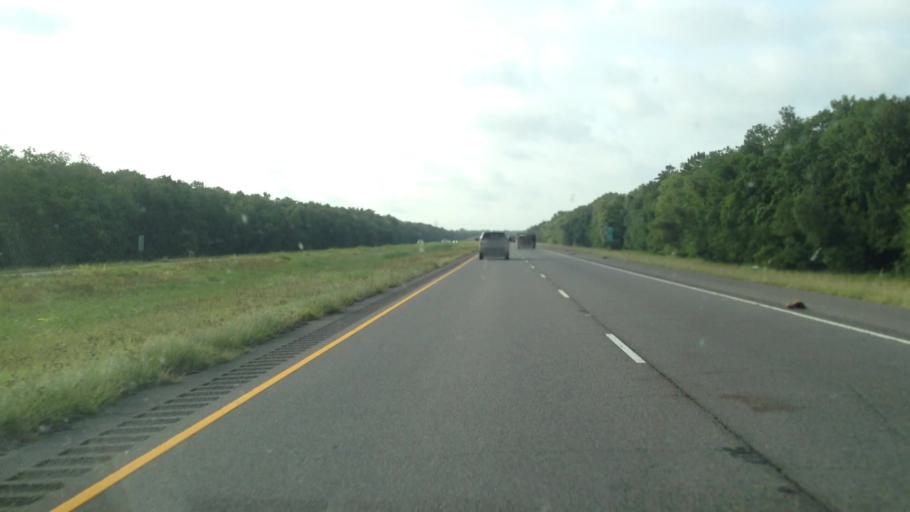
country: US
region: Louisiana
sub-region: Avoyelles Parish
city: Bunkie
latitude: 30.9092
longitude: -92.2383
